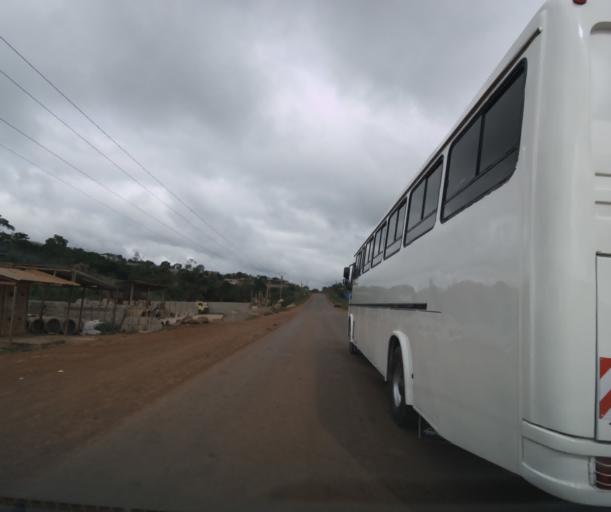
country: CM
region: Centre
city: Yaounde
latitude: 3.7947
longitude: 11.4822
